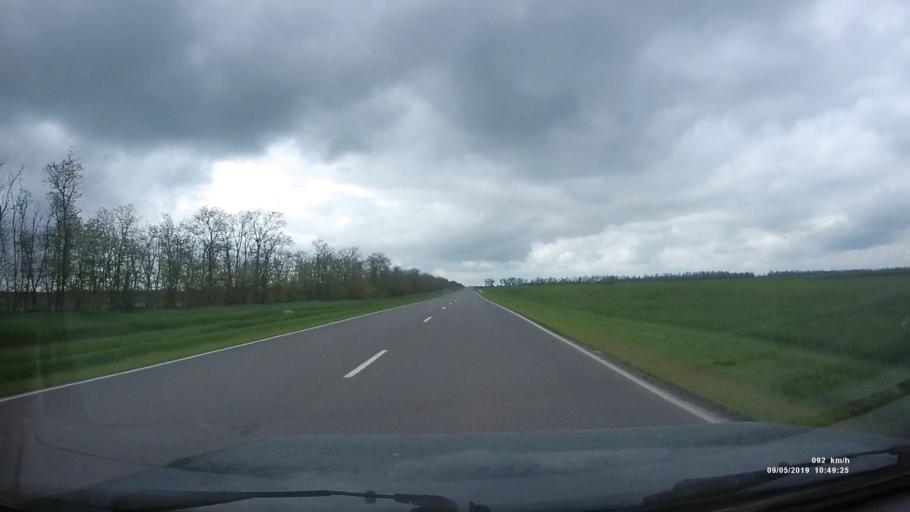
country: RU
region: Rostov
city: Peshkovo
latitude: 46.9429
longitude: 39.3562
